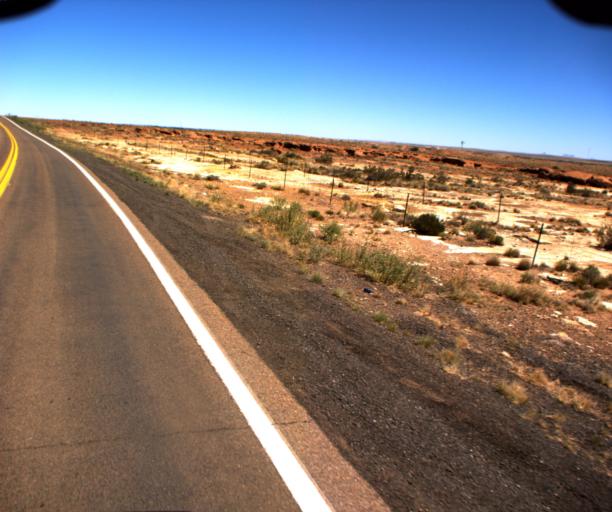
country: US
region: Arizona
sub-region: Navajo County
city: Winslow
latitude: 34.9705
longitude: -110.6476
